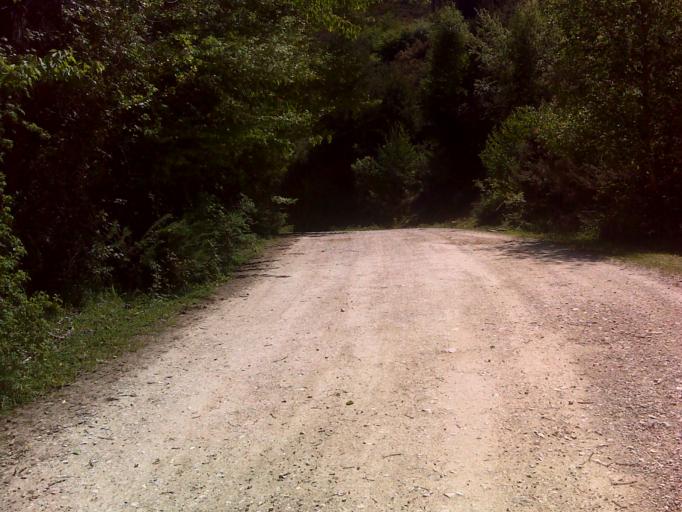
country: ES
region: Cantabria
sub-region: Provincia de Cantabria
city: San Pedro del Romeral
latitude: 43.0532
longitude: -3.7325
